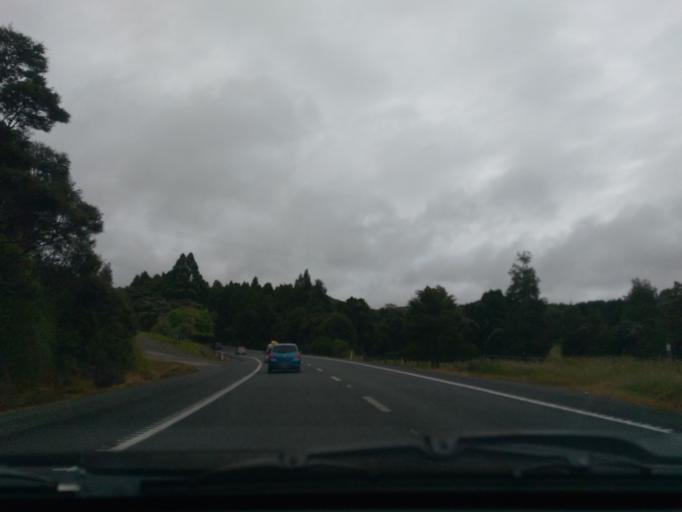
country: NZ
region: Auckland
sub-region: Auckland
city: Wellsford
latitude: -36.1106
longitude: 174.4340
